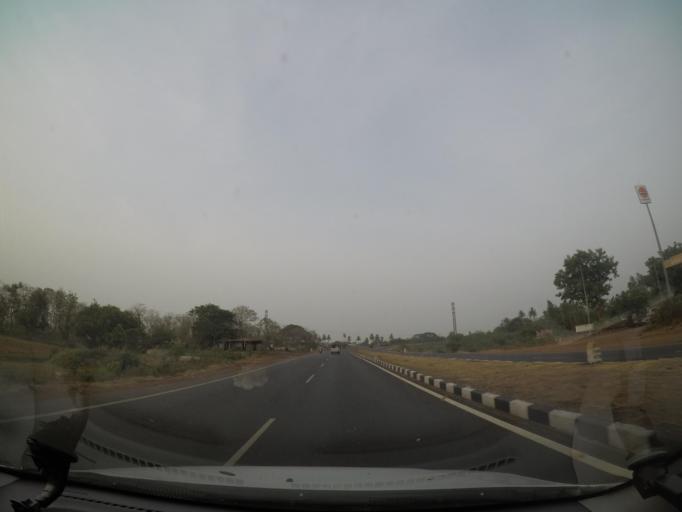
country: IN
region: Andhra Pradesh
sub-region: Krishna
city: Gannavaram
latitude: 16.6125
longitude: 80.9232
